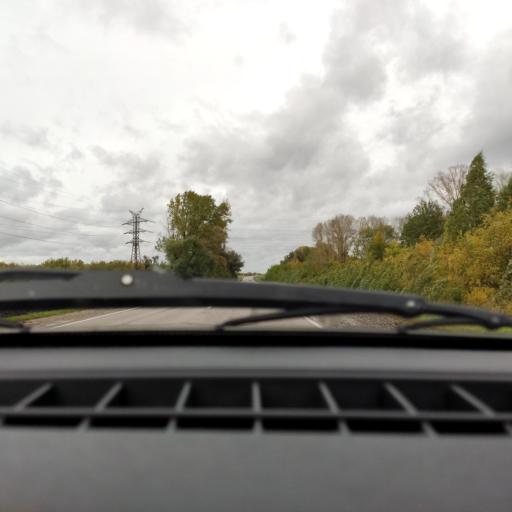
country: RU
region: Bashkortostan
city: Chishmy
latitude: 54.5192
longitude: 55.2971
